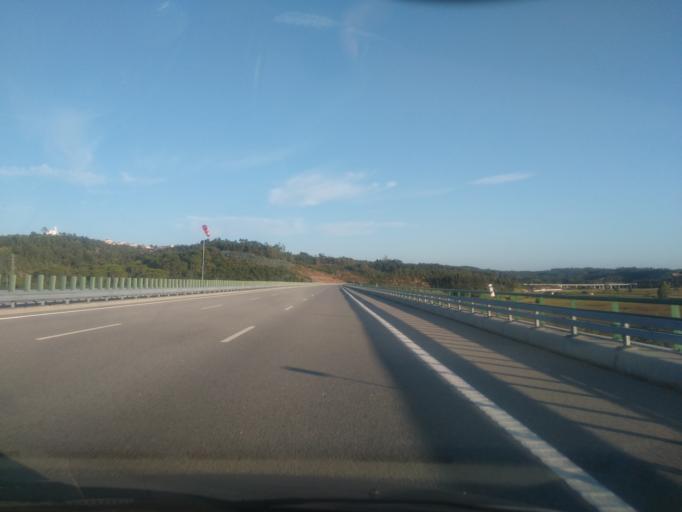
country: PT
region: Coimbra
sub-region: Figueira da Foz
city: Alhadas
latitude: 40.1400
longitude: -8.7495
